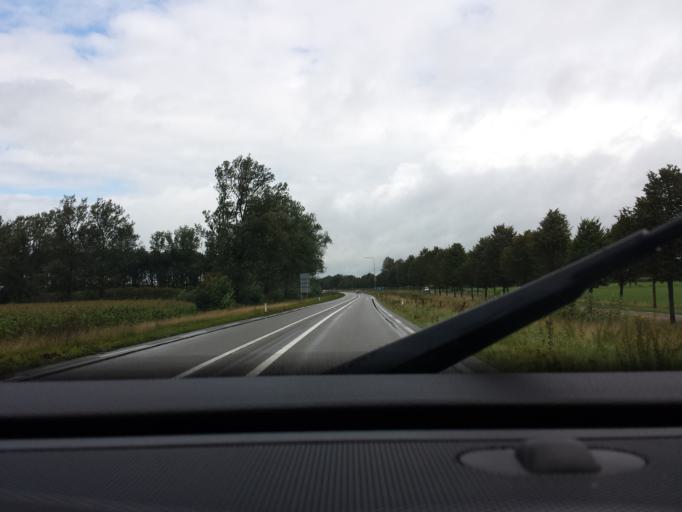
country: NL
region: Gelderland
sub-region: Gemeente Lochem
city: Laren
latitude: 52.2567
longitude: 6.3996
